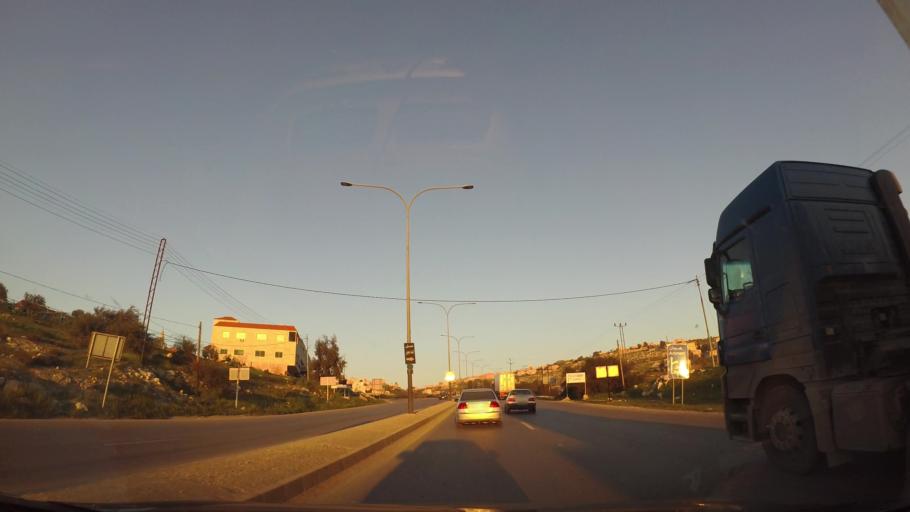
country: JO
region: Amman
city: Umm as Summaq
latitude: 31.8610
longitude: 35.8056
